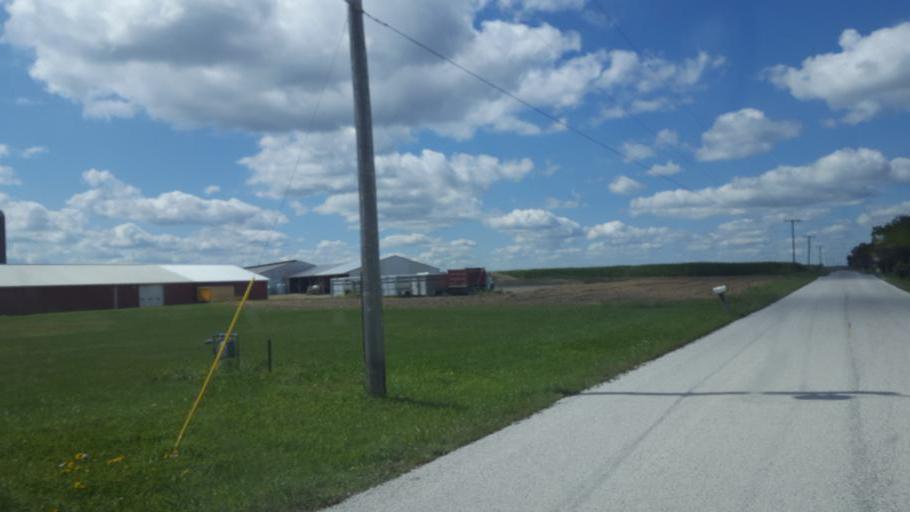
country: US
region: Ohio
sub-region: Wayne County
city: West Salem
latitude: 40.9740
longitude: -82.2153
